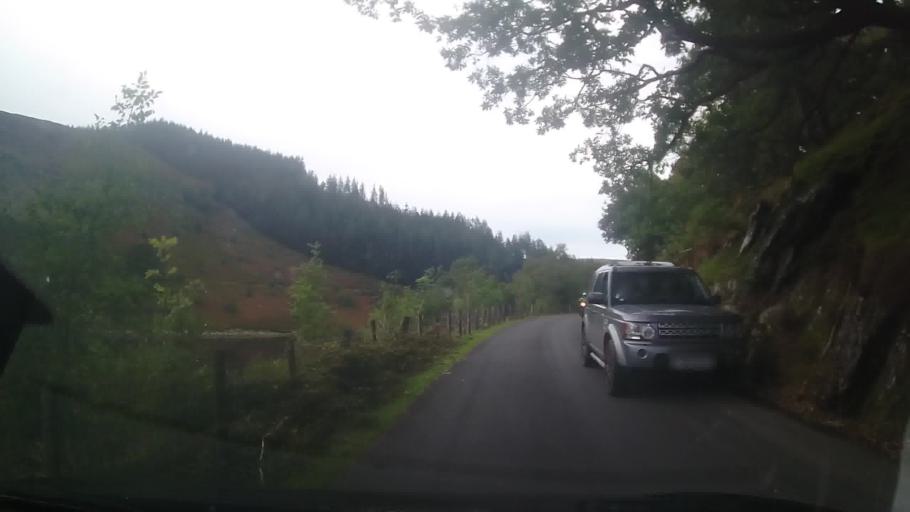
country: GB
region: Wales
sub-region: Sir Powys
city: Rhayader
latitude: 52.2831
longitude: -3.5946
